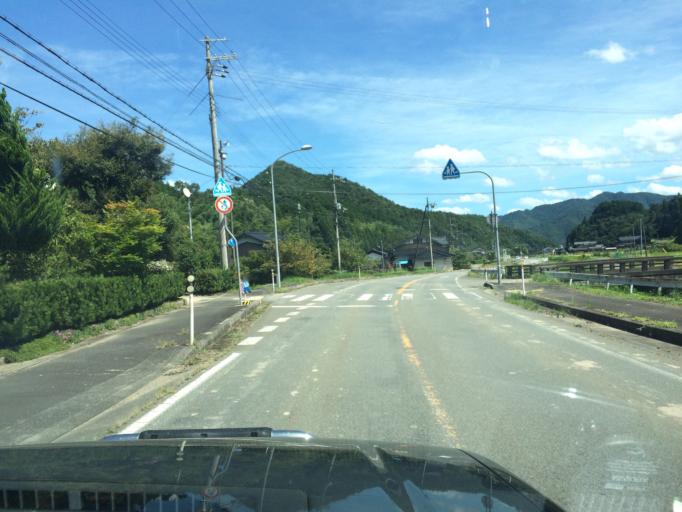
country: JP
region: Hyogo
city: Toyooka
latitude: 35.4633
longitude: 134.8324
